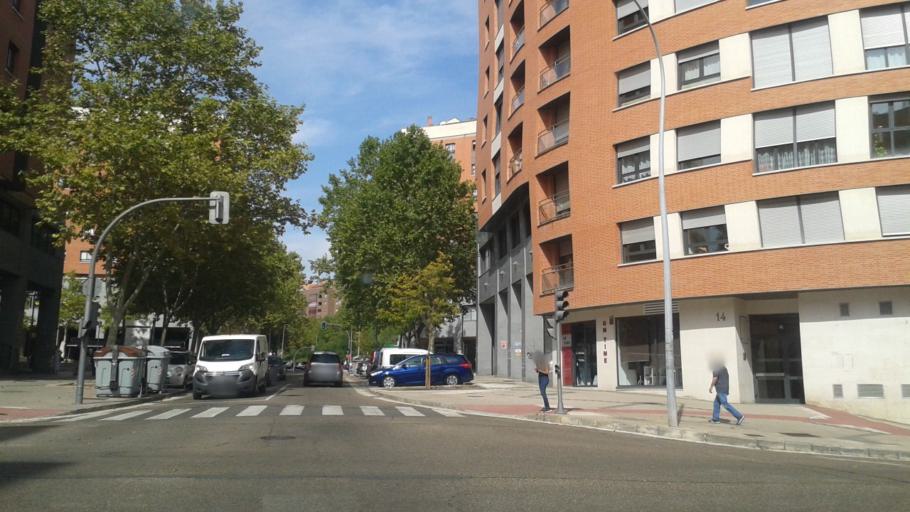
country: ES
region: Castille and Leon
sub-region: Provincia de Valladolid
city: Zaratan
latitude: 41.6358
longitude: -4.7590
